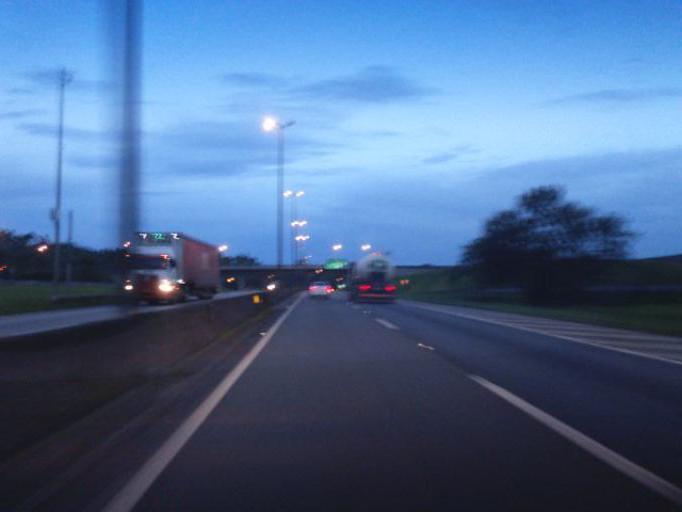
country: BR
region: Santa Catarina
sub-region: Joinville
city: Joinville
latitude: -26.4373
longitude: -48.8080
